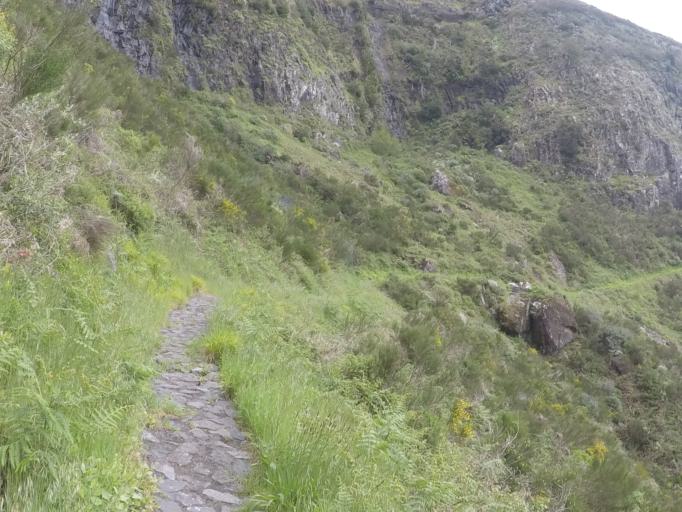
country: PT
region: Madeira
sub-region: Camara de Lobos
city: Curral das Freiras
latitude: 32.7400
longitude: -17.0013
